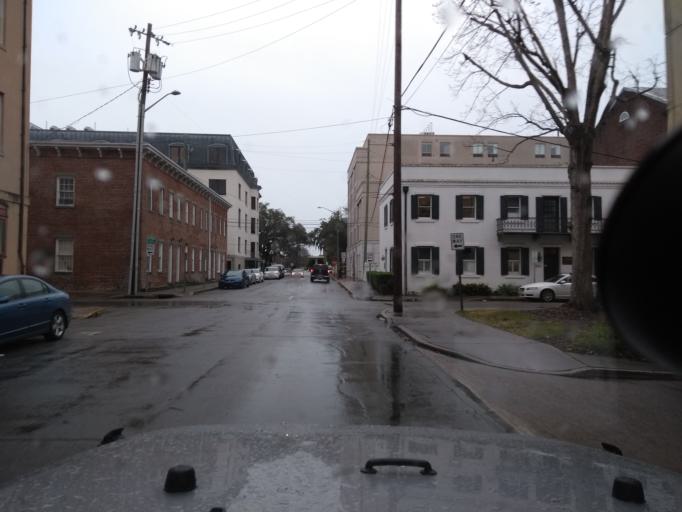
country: US
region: Georgia
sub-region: Chatham County
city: Savannah
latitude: 32.0788
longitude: -81.0958
